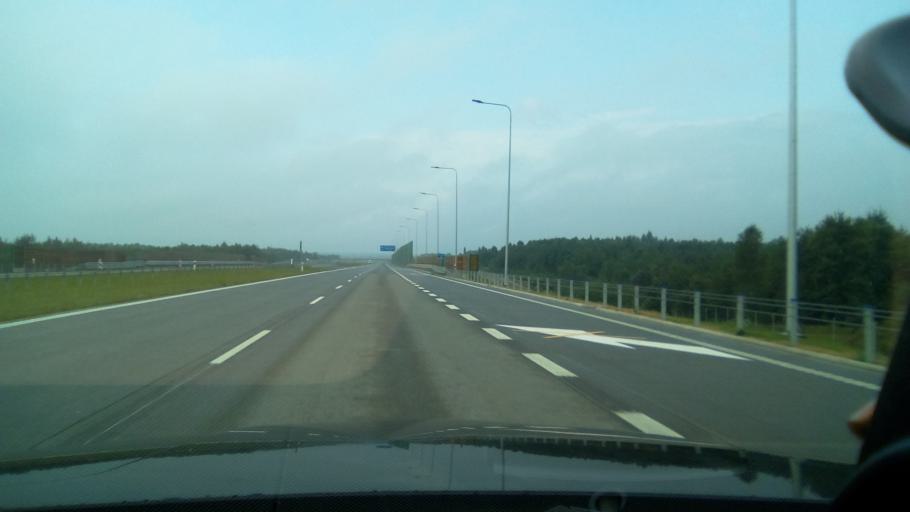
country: PL
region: Silesian Voivodeship
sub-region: Powiat klobucki
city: Kalej
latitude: 50.8101
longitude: 19.0160
